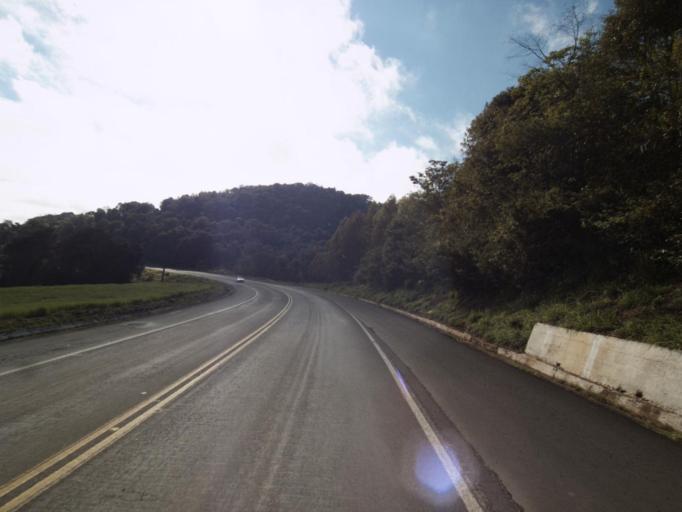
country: BR
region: Rio Grande do Sul
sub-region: Frederico Westphalen
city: Frederico Westphalen
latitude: -27.1576
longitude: -53.2174
